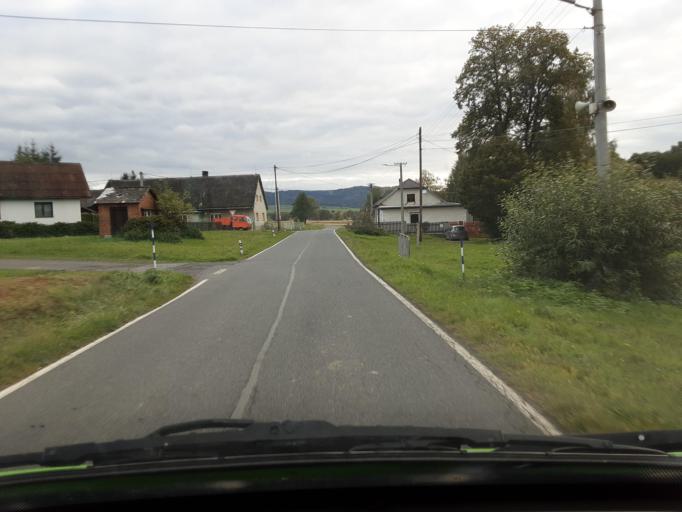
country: CZ
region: Plzensky
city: Janovice nad Uhlavou
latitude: 49.4136
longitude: 13.1642
